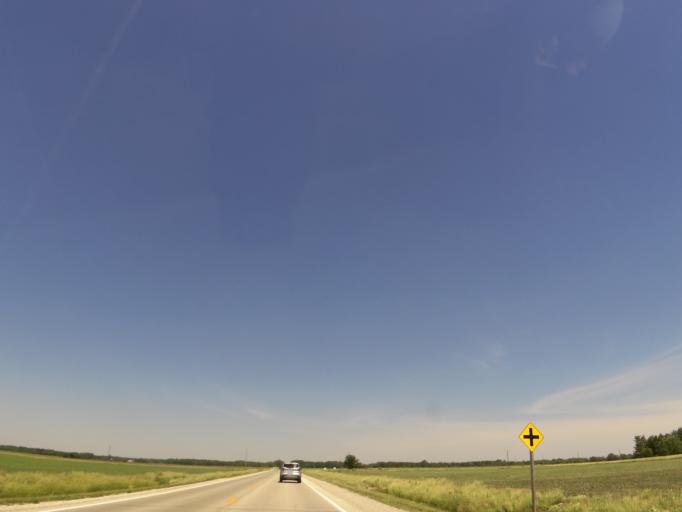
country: US
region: Illinois
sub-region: Iroquois County
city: Milford
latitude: 40.5868
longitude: -87.6944
